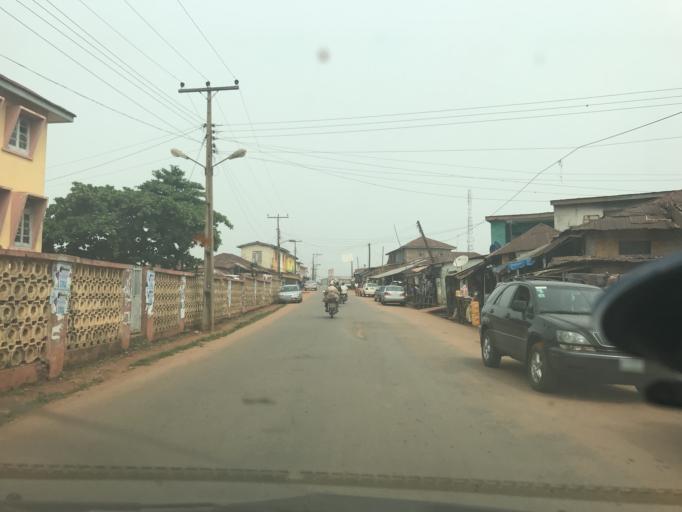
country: NG
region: Ogun
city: Ilaro
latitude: 6.8855
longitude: 3.0204
